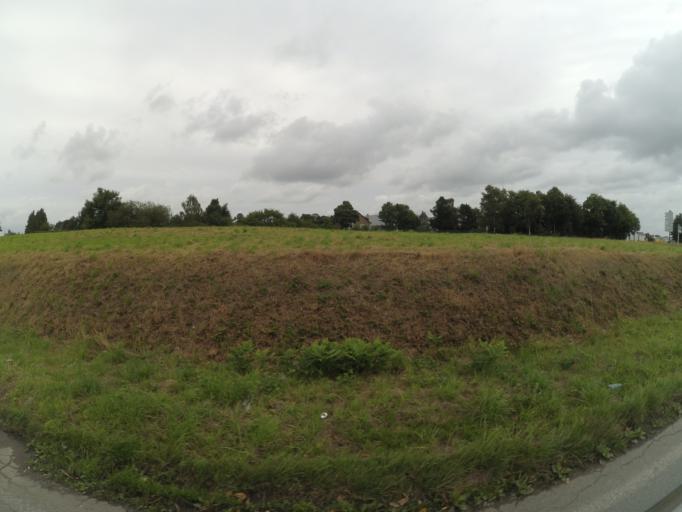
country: FR
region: Brittany
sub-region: Departement des Cotes-d'Armor
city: Ploumagoar
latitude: 48.5521
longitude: -3.1238
